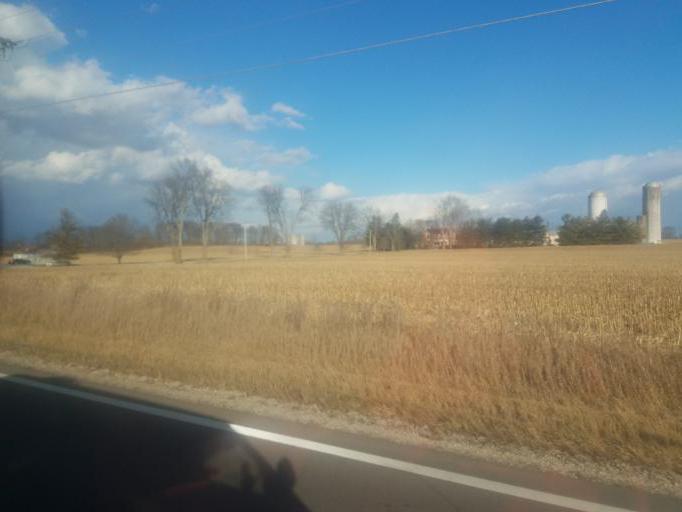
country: US
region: Ohio
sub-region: Marion County
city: Prospect
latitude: 40.3742
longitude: -83.1481
